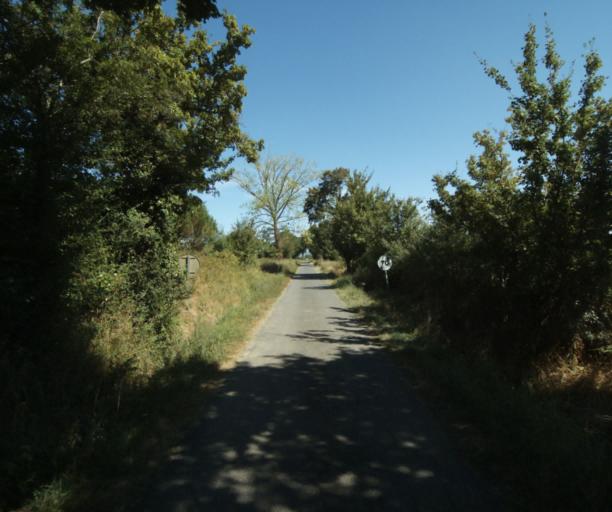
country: FR
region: Midi-Pyrenees
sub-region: Departement de la Haute-Garonne
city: Auriac-sur-Vendinelle
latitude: 43.5199
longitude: 1.8926
